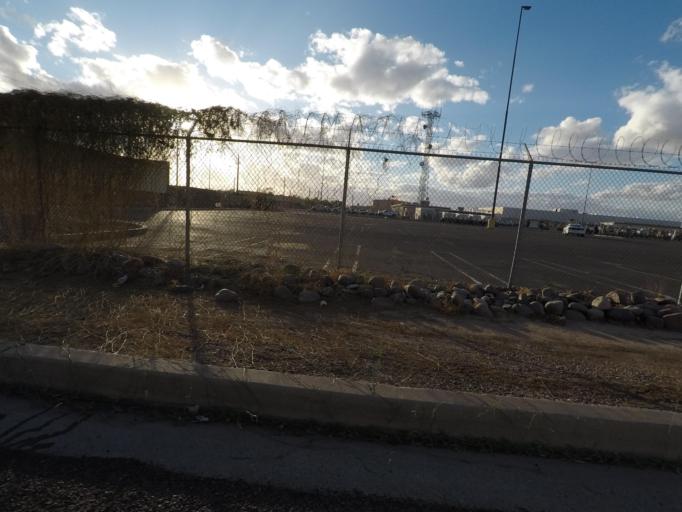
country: US
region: Arizona
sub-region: Maricopa County
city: Glendale
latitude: 33.4998
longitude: -112.1451
